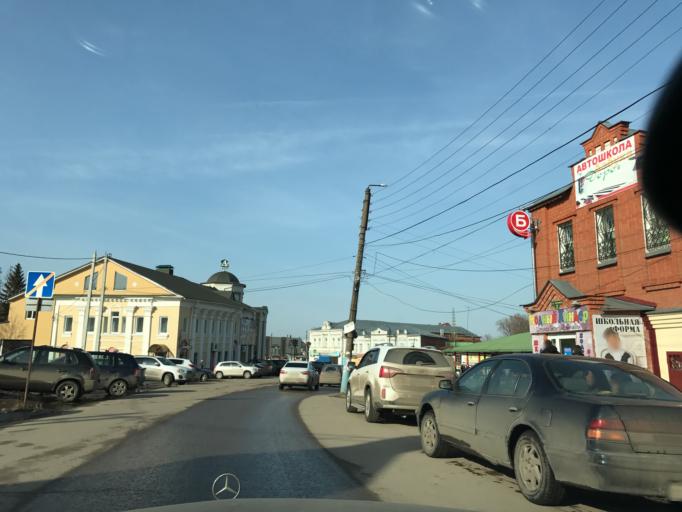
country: RU
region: Nizjnij Novgorod
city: Pavlovo
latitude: 55.9651
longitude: 43.0679
